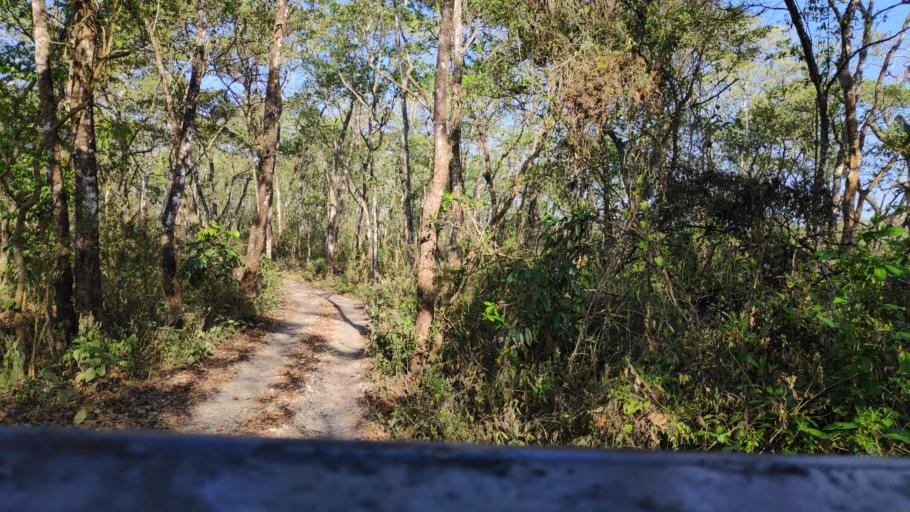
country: NP
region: Central Region
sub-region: Narayani Zone
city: Bharatpur
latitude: 27.5611
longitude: 84.5306
